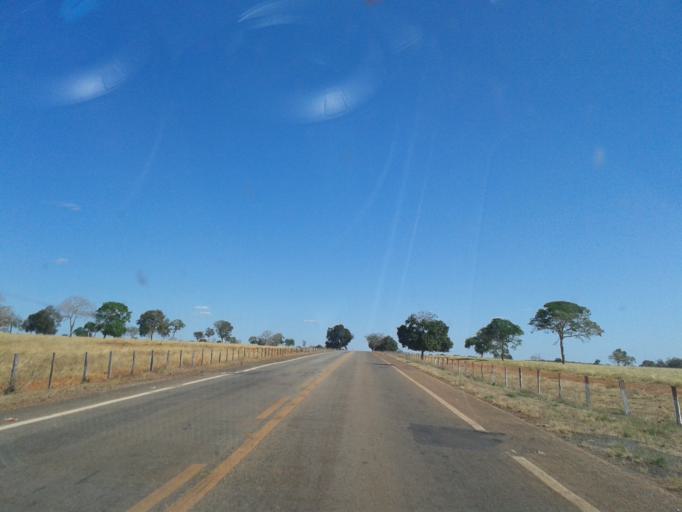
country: BR
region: Goias
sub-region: Crixas
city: Crixas
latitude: -14.1569
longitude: -50.3637
